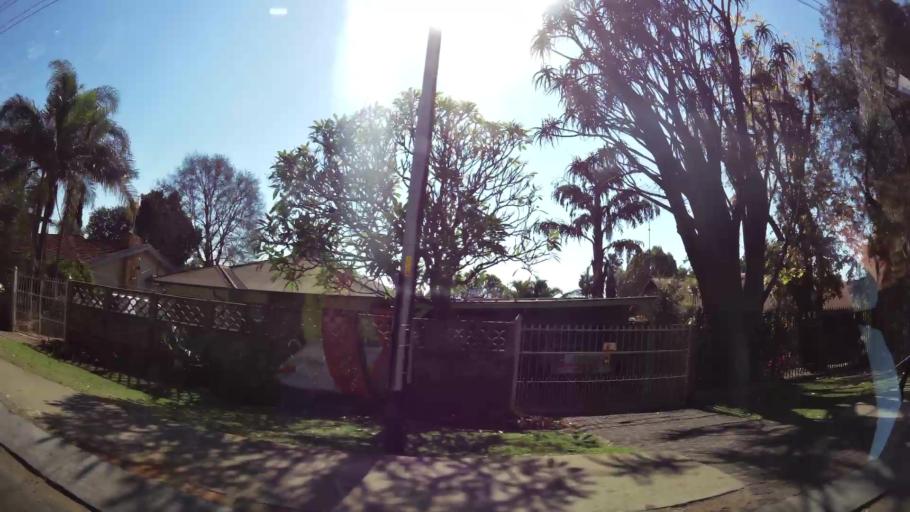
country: ZA
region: Gauteng
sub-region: City of Tshwane Metropolitan Municipality
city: Pretoria
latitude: -25.6862
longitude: 28.2228
